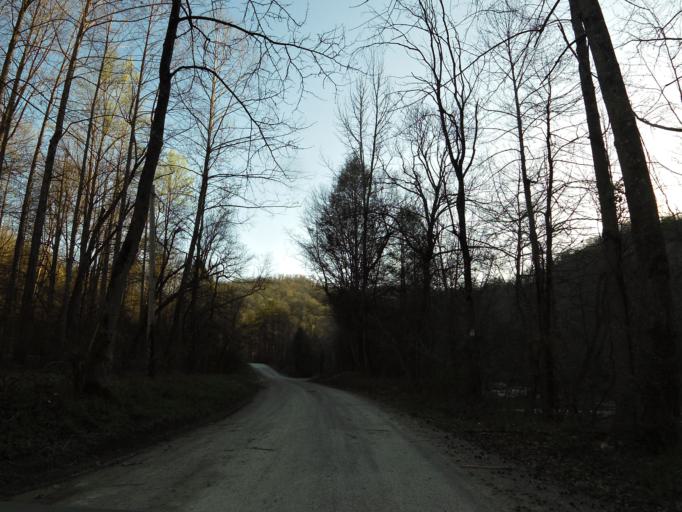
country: US
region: Tennessee
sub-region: Campbell County
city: Caryville
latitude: 36.2634
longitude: -84.3507
